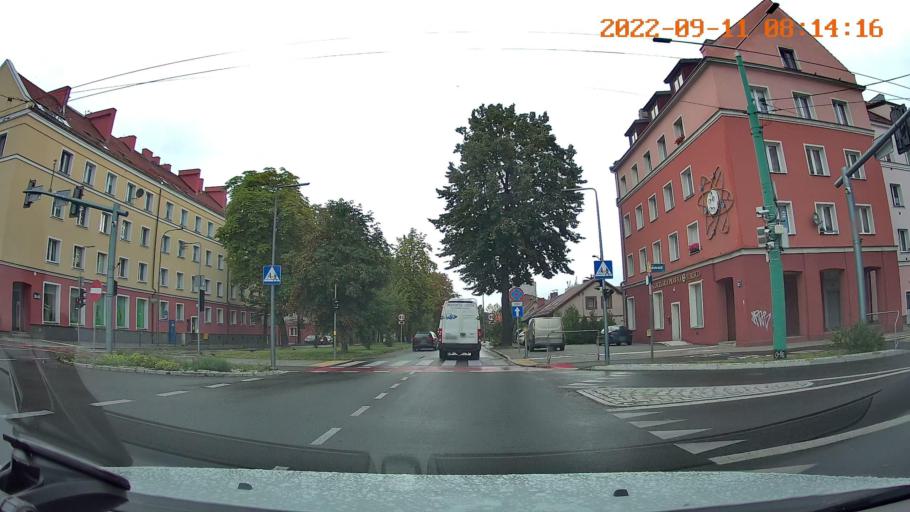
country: PL
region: Silesian Voivodeship
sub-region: Tychy
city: Tychy
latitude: 50.1236
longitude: 18.9871
